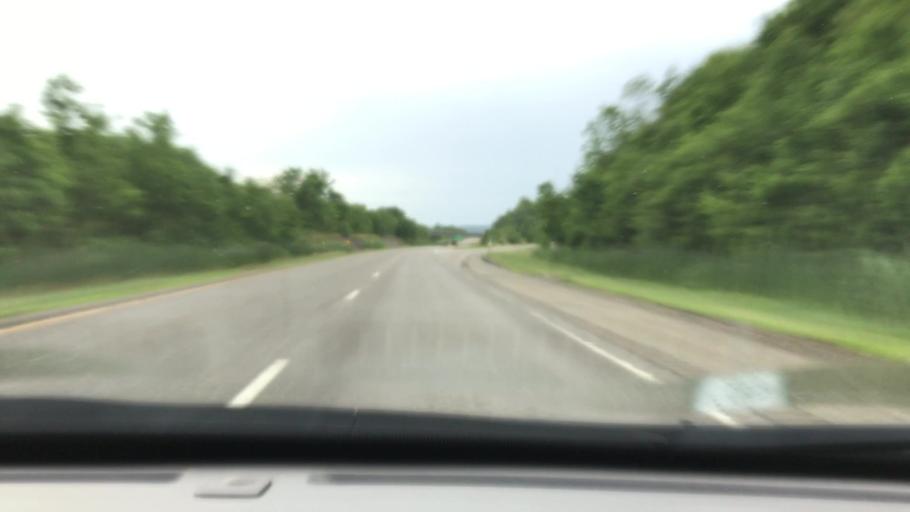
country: US
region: New York
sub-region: Erie County
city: North Boston
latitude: 42.6259
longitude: -78.7640
